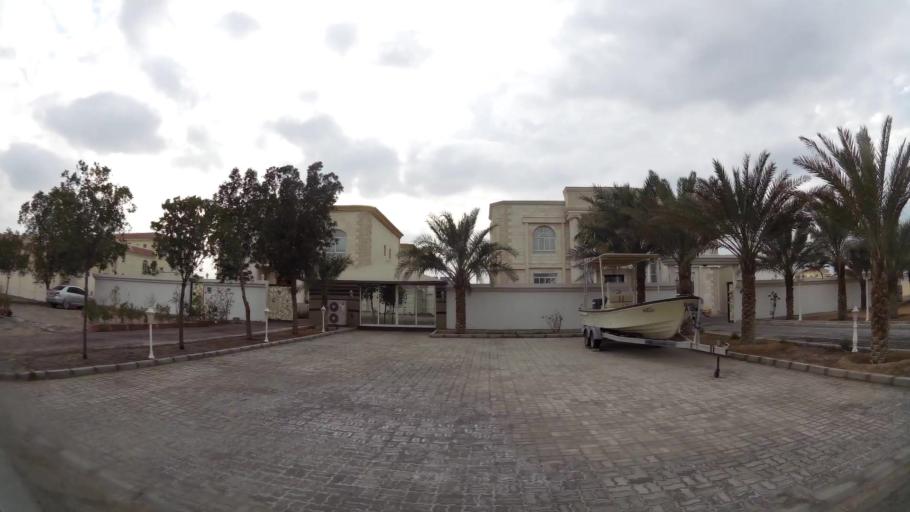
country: AE
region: Abu Dhabi
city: Abu Dhabi
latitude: 24.3598
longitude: 54.5453
